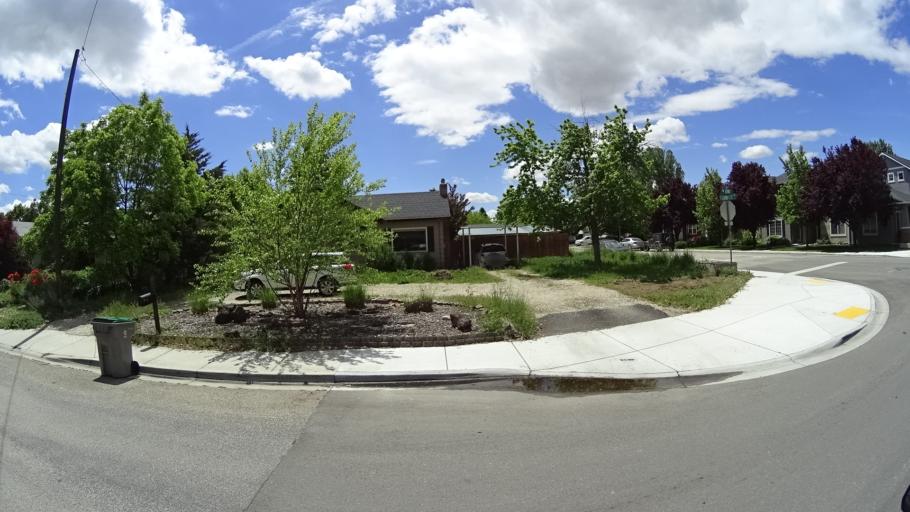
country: US
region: Idaho
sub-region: Ada County
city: Boise
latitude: 43.5844
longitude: -116.1907
